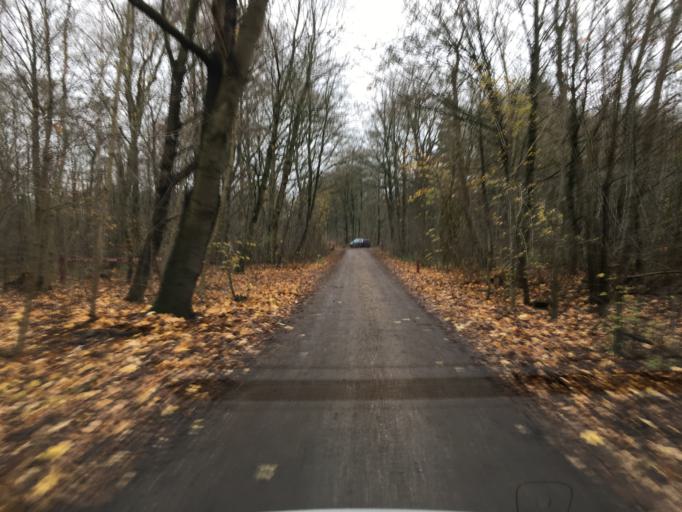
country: DK
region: South Denmark
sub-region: Tonder Kommune
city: Tonder
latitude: 54.9629
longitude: 8.8562
